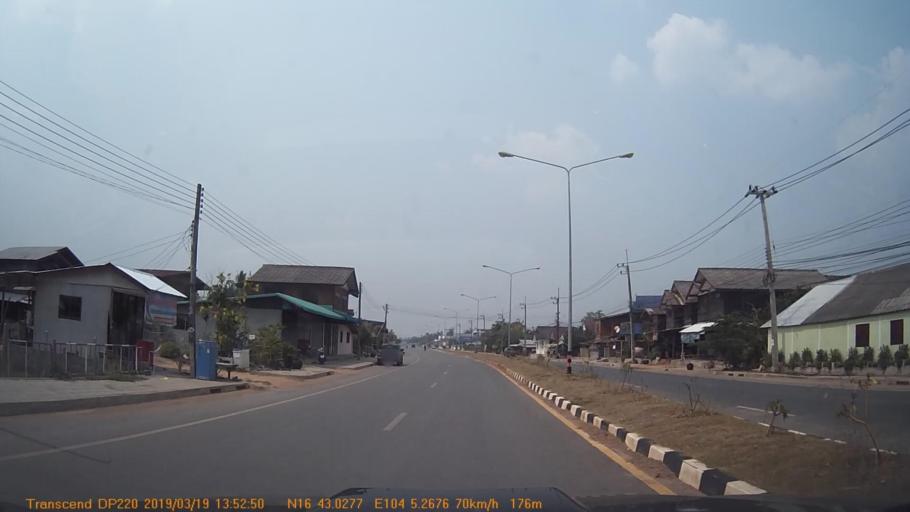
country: TH
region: Kalasin
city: Khao Wong
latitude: 16.7176
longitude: 104.0877
